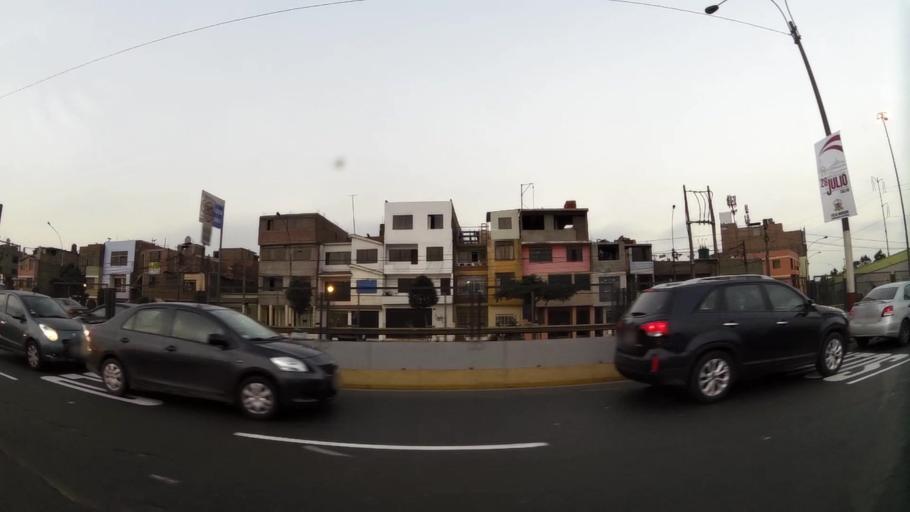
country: PE
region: Callao
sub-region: Callao
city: Callao
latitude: -12.0354
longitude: -77.0997
